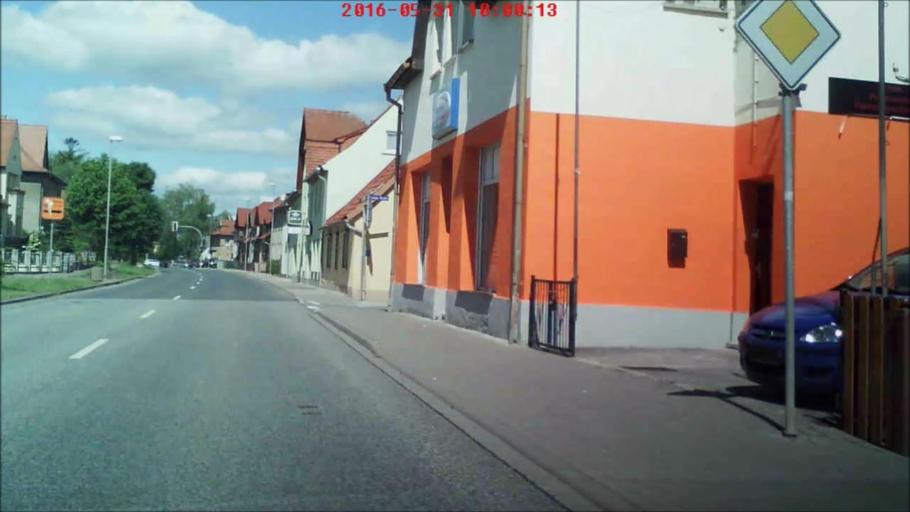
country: DE
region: Thuringia
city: Heldrungen
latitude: 51.2997
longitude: 11.2152
